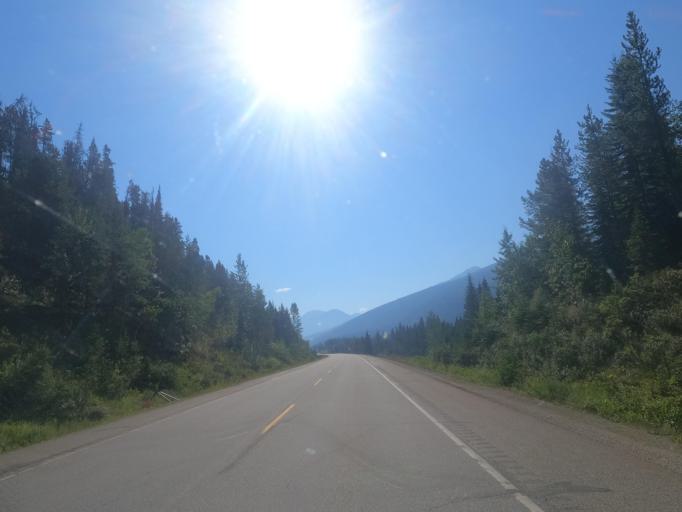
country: CA
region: Alberta
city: Jasper Park Lodge
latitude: 52.8889
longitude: -118.7252
